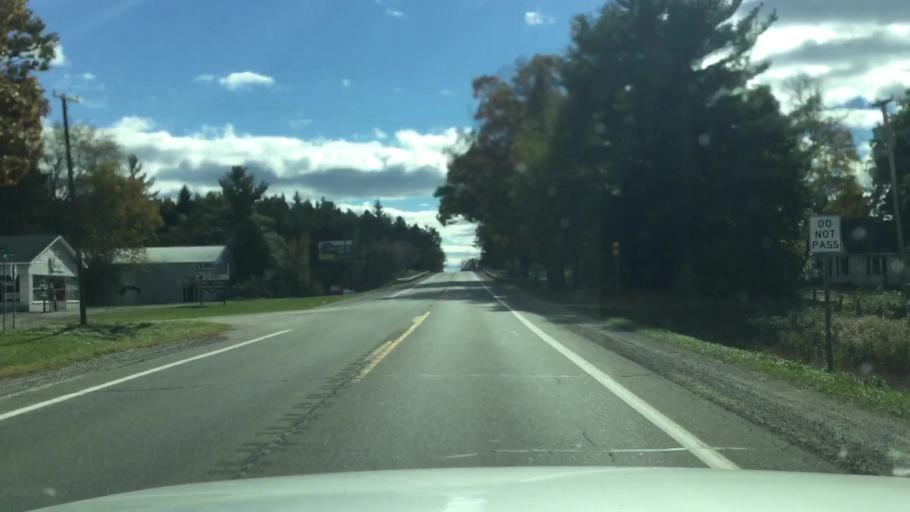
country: US
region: Michigan
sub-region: Lapeer County
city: Barnes Lake-Millers Lake
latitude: 43.1386
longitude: -83.3108
